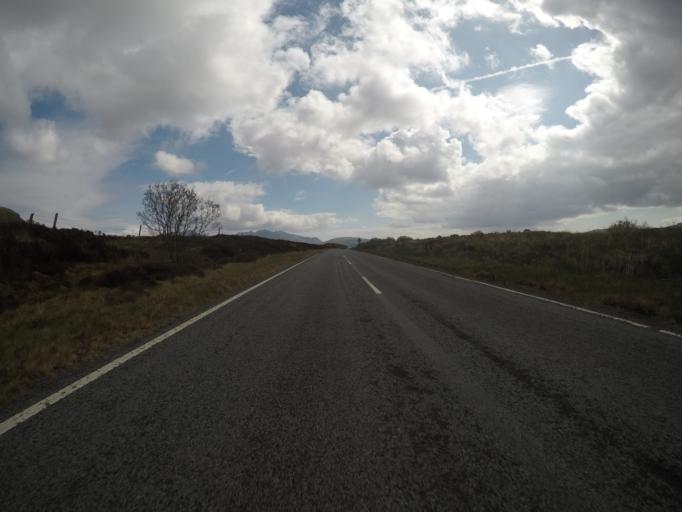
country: GB
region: Scotland
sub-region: Highland
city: Isle of Skye
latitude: 57.3155
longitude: -6.3204
